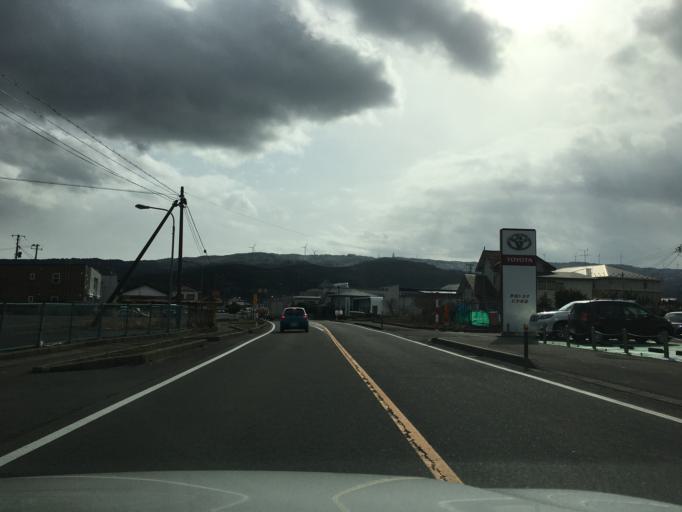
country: JP
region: Yamagata
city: Yuza
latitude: 39.2859
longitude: 139.9579
